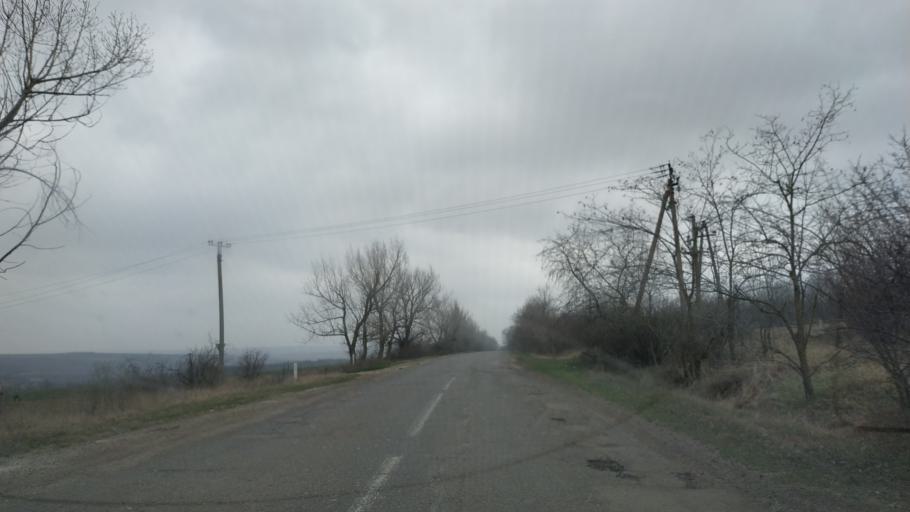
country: MD
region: Gagauzia
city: Bugeac
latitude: 46.3510
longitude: 28.7870
